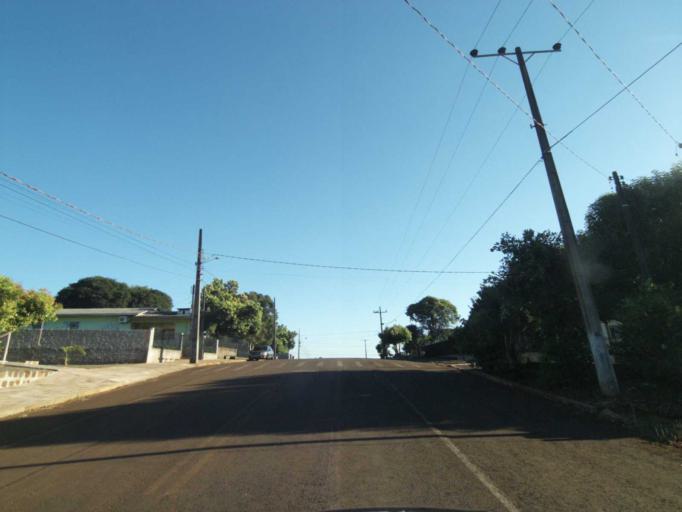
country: BR
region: Parana
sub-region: Coronel Vivida
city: Coronel Vivida
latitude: -25.9585
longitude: -52.8145
